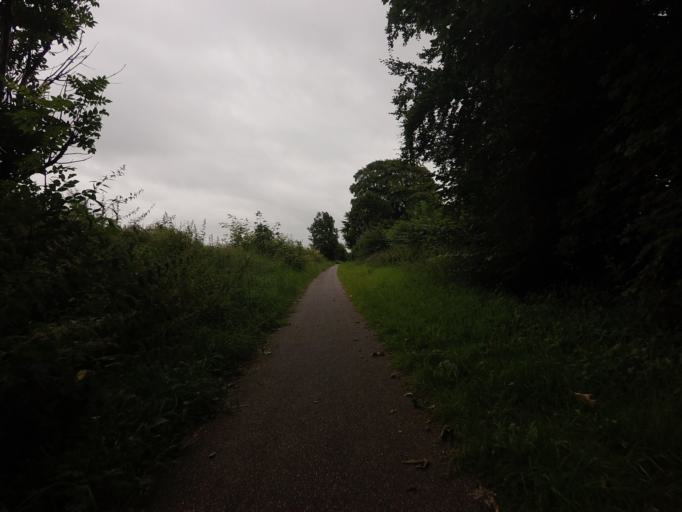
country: DK
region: Central Jutland
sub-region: Horsens Kommune
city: Braedstrup
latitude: 56.0183
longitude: 9.5822
